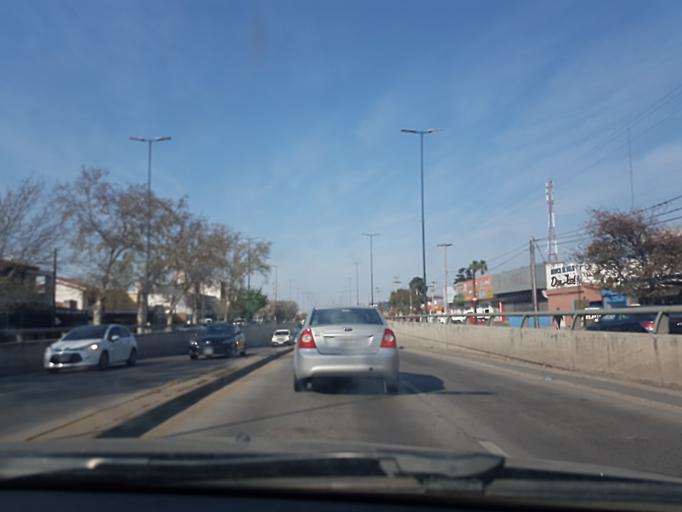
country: AR
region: Cordoba
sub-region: Departamento de Capital
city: Cordoba
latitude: -31.3679
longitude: -64.2053
